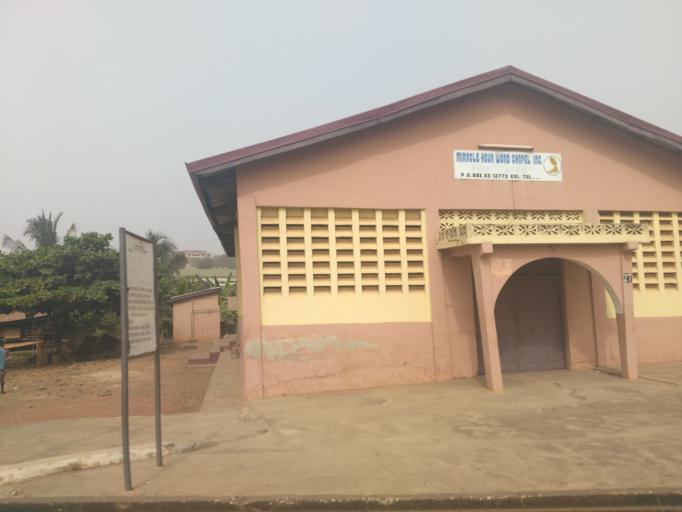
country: GH
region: Ashanti
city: Kumasi
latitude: 6.7112
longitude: -1.6394
